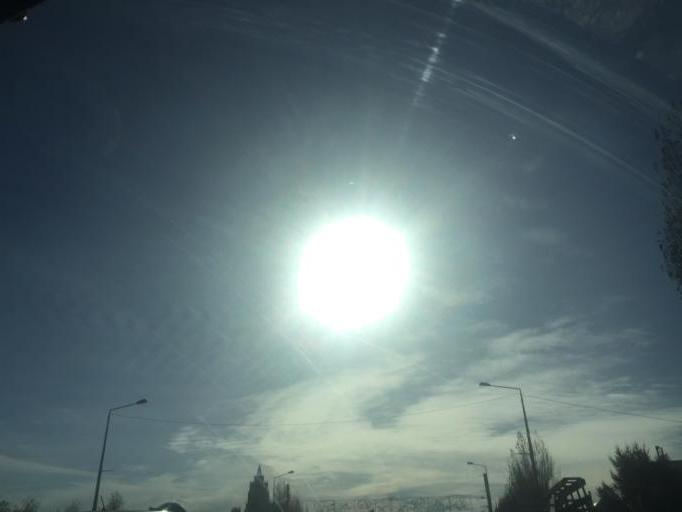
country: KZ
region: Astana Qalasy
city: Astana
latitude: 51.1488
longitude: 71.4124
